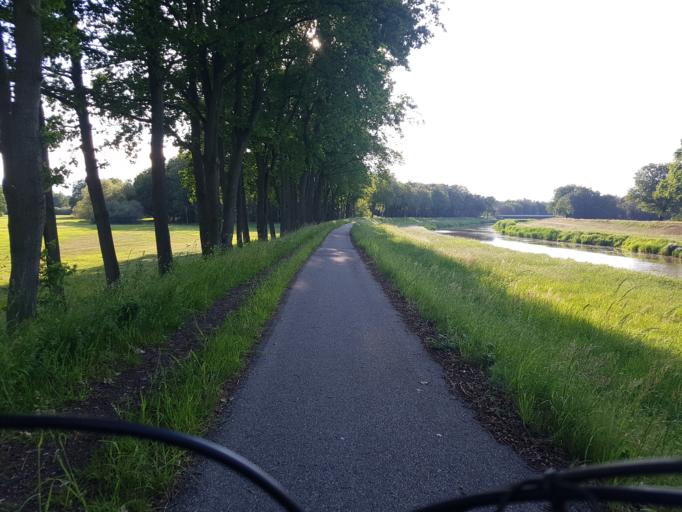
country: DE
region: Brandenburg
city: Bad Liebenwerda
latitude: 51.4822
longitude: 13.4418
